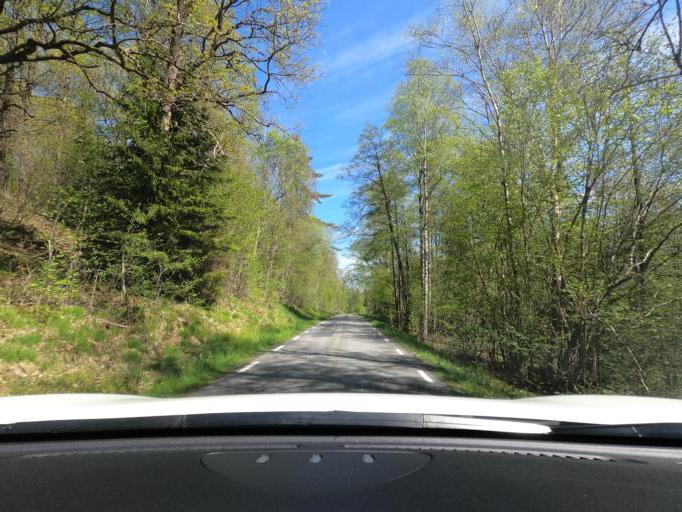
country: SE
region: Vaestra Goetaland
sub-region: Marks Kommun
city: Horred
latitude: 57.4359
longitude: 12.4172
